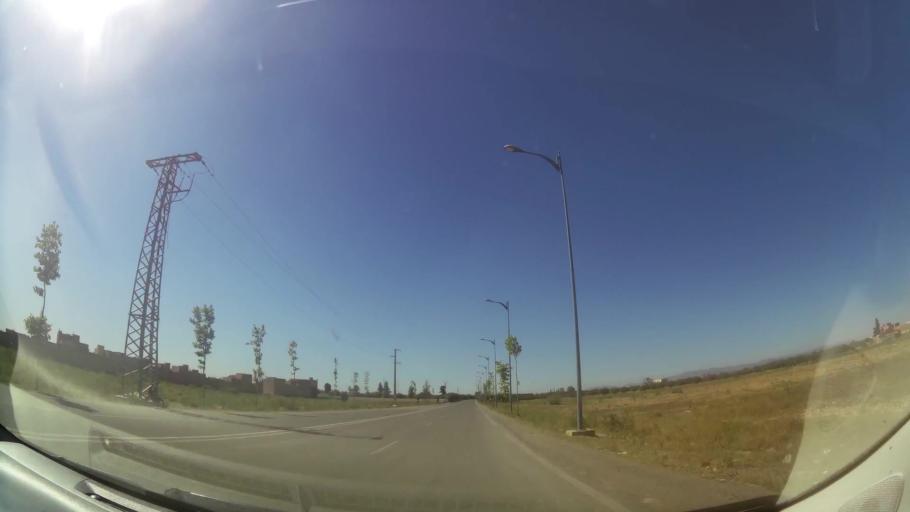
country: MA
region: Oriental
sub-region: Oujda-Angad
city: Oujda
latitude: 34.7107
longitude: -1.8612
